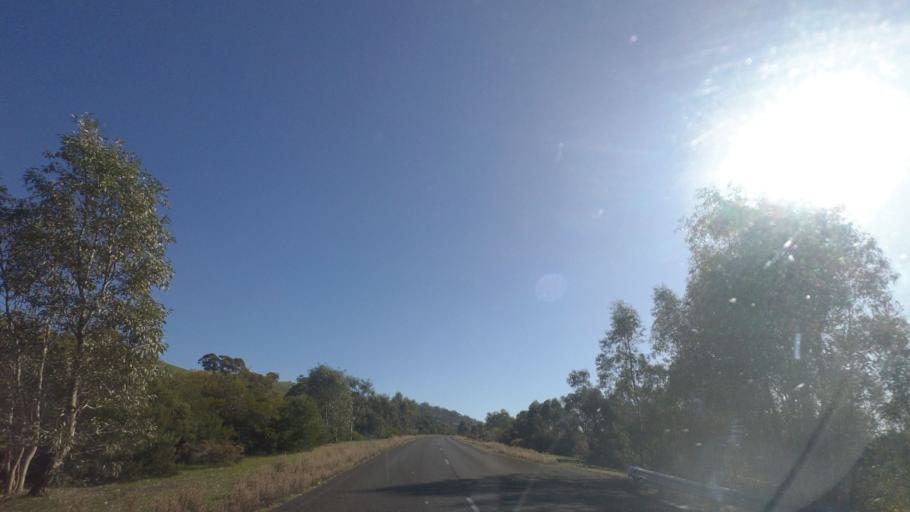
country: AU
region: Victoria
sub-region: Mount Alexander
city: Castlemaine
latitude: -37.0459
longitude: 144.2833
